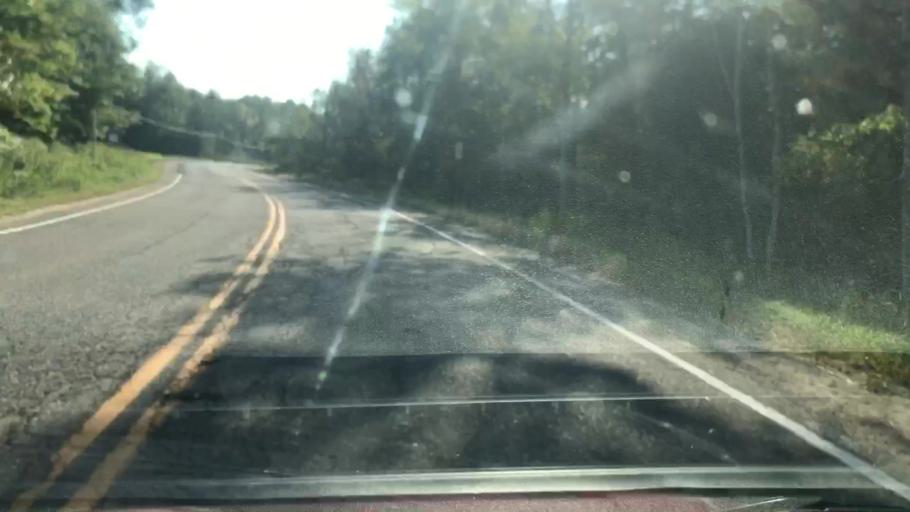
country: US
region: Michigan
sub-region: Chippewa County
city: Sault Ste. Marie
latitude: 46.2912
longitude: -84.0400
